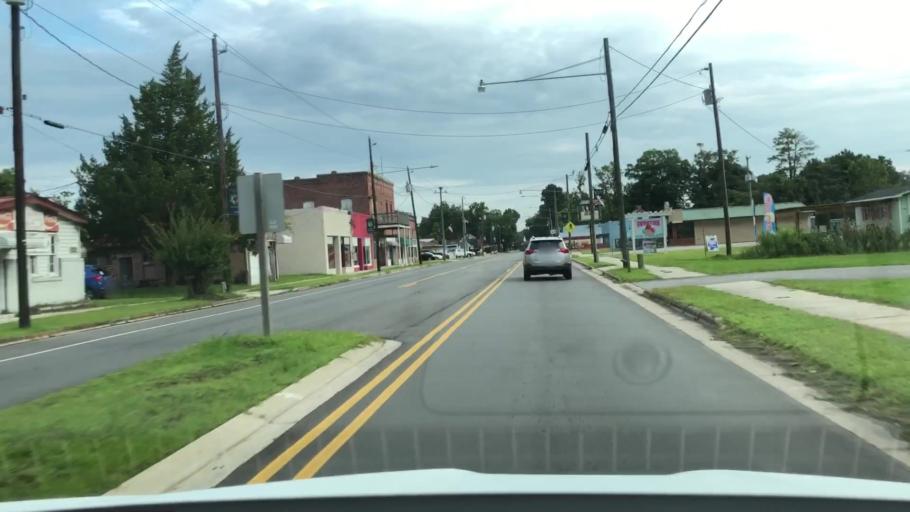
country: US
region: North Carolina
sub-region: Jones County
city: Maysville
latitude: 34.9041
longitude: -77.2315
